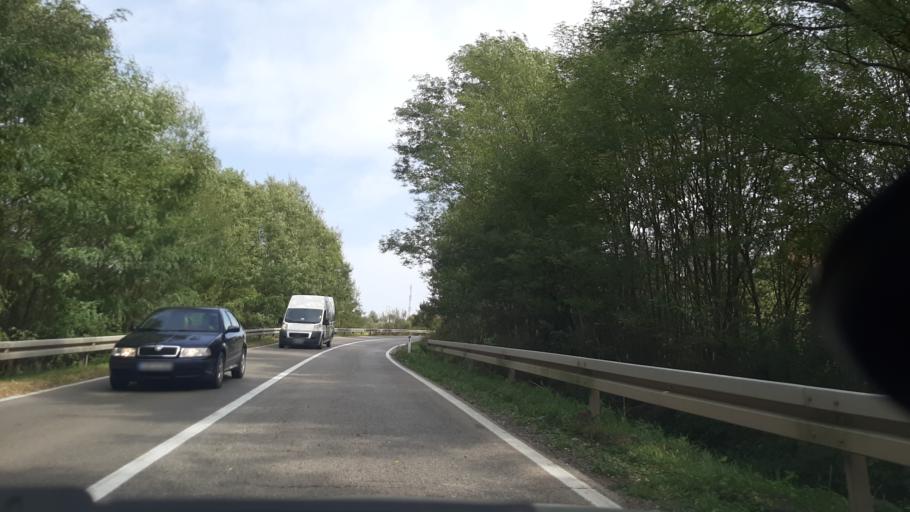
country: BA
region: Republika Srpska
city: Laktasi
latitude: 44.8688
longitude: 17.3486
